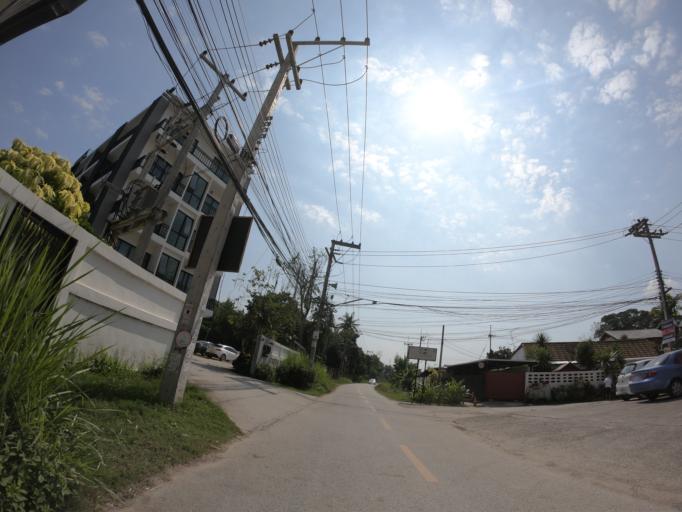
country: TH
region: Chiang Mai
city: Chiang Mai
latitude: 18.7840
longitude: 98.9702
